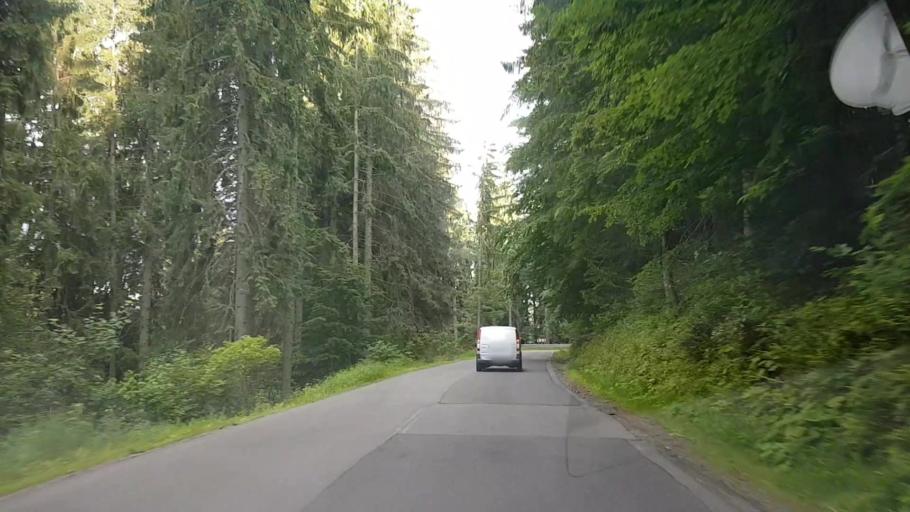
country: RO
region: Harghita
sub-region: Comuna Remetea
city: Remetea
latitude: 46.6722
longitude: 25.3417
